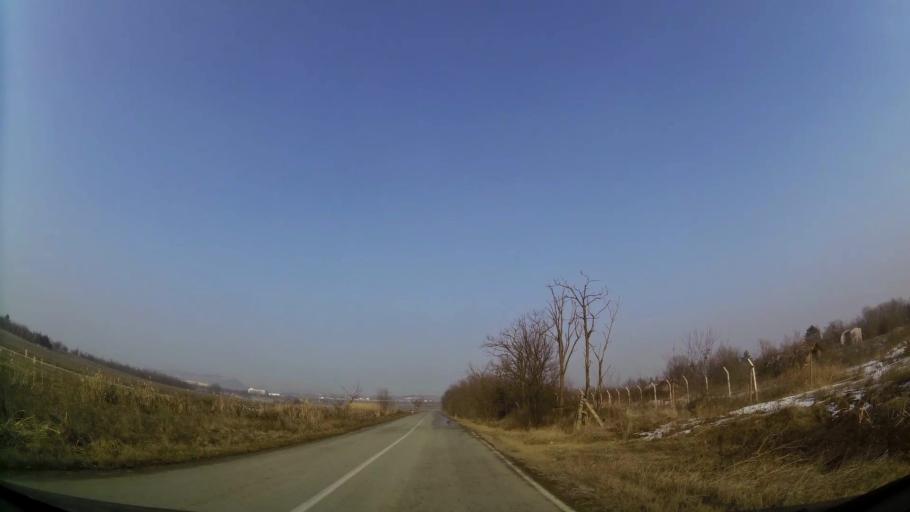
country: MK
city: Kadino
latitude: 41.9761
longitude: 21.6106
